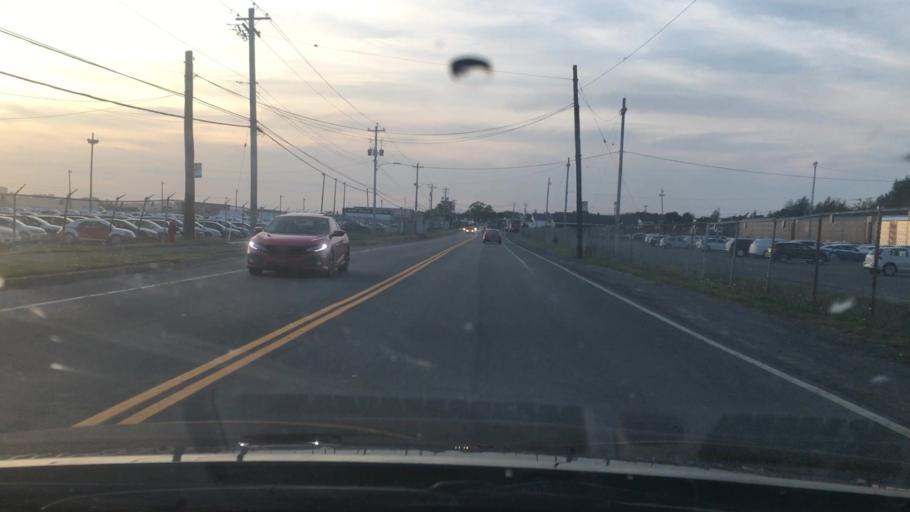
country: CA
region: Nova Scotia
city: Cole Harbour
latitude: 44.6214
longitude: -63.5075
